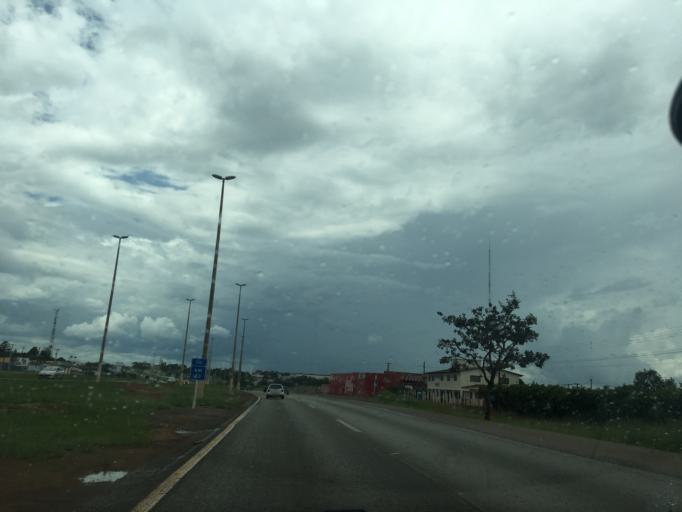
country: BR
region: Goias
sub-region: Luziania
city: Luziania
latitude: -16.2356
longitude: -47.9124
